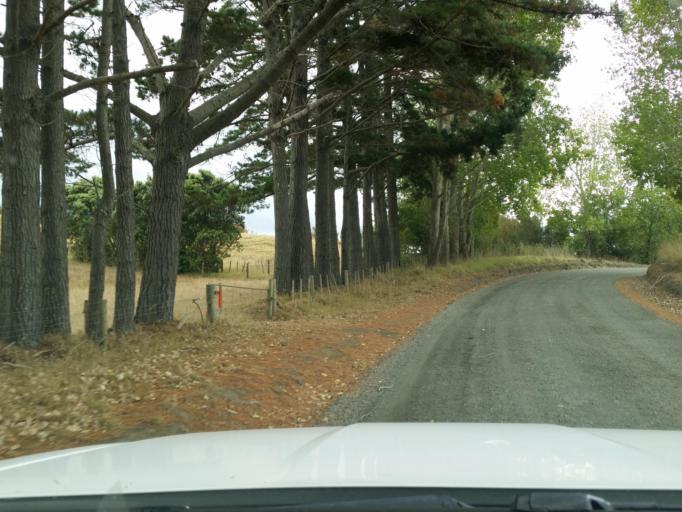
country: NZ
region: Auckland
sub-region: Auckland
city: Wellsford
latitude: -36.3283
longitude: 174.1431
